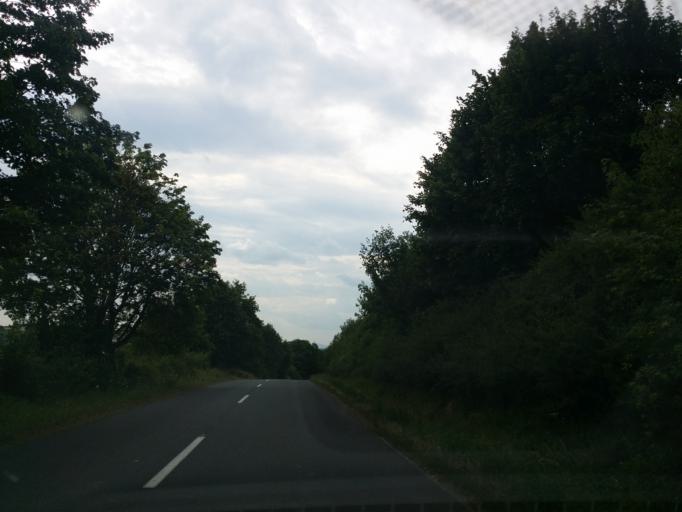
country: HU
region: Nograd
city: Bercel
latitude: 47.9771
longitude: 19.4073
